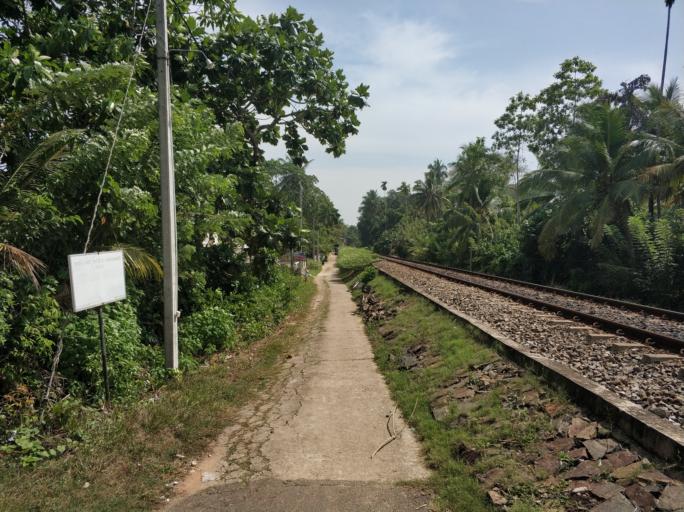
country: LK
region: Southern
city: Weligama
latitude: 5.9654
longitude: 80.4024
